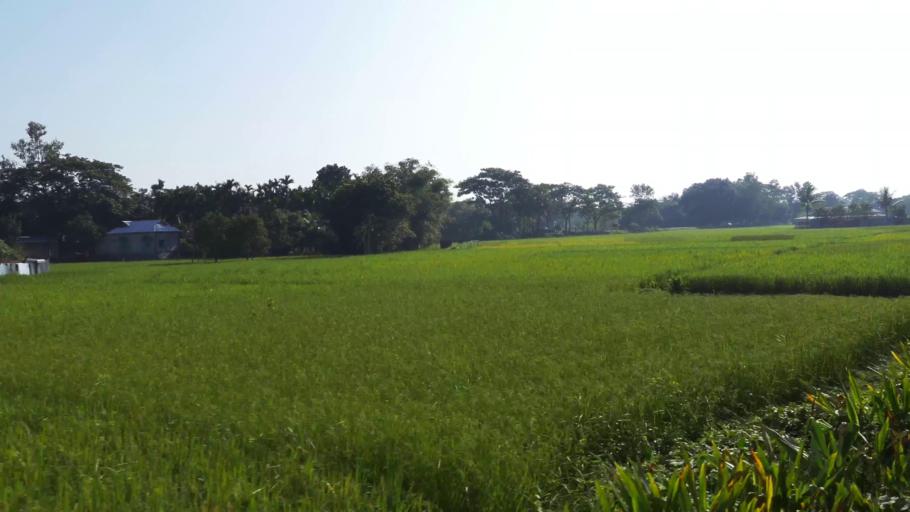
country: BD
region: Dhaka
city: Muktagacha
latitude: 24.8109
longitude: 90.2954
